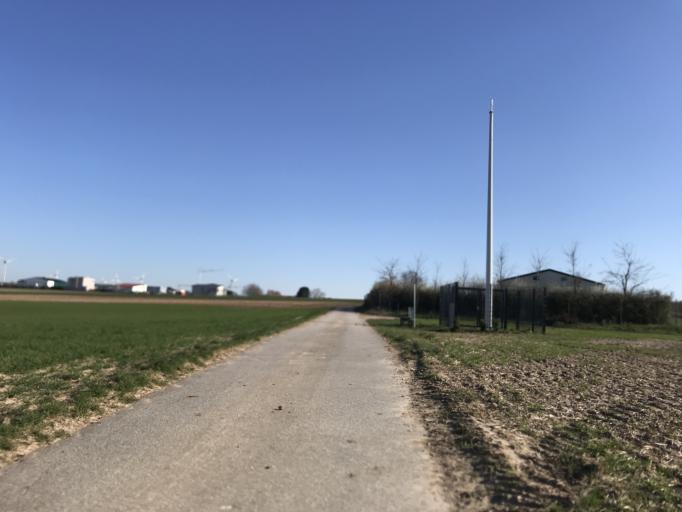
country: DE
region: Rheinland-Pfalz
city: Klein-Winternheim
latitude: 49.9531
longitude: 8.2106
